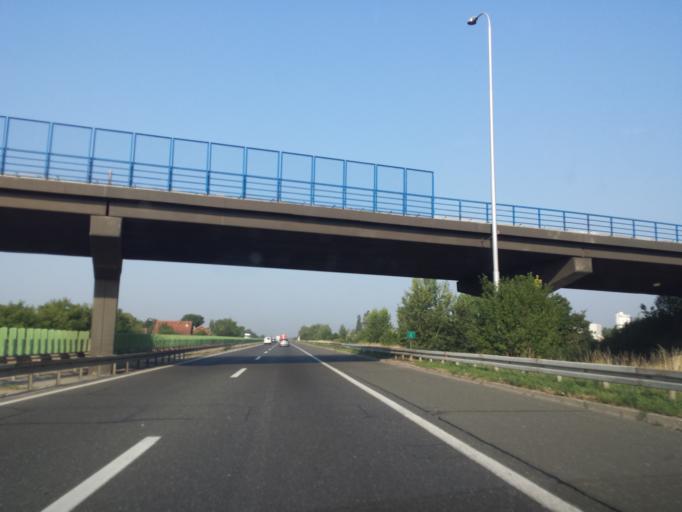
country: HR
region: Grad Zagreb
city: Novi Zagreb
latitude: 45.7522
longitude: 15.9643
